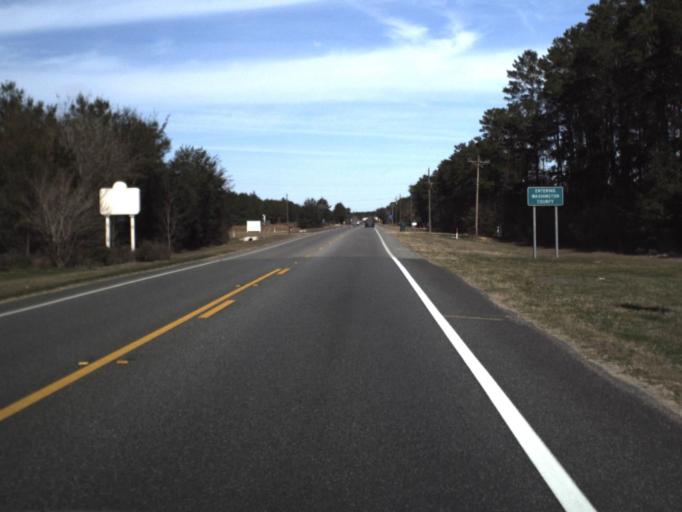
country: US
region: Florida
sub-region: Bay County
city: Lynn Haven
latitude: 30.4389
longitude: -85.6881
